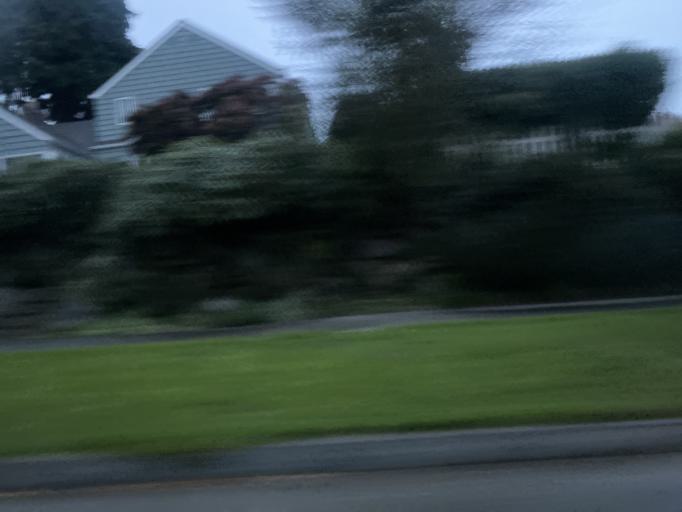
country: US
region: Washington
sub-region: King County
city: Seattle
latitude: 47.6440
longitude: -122.3942
